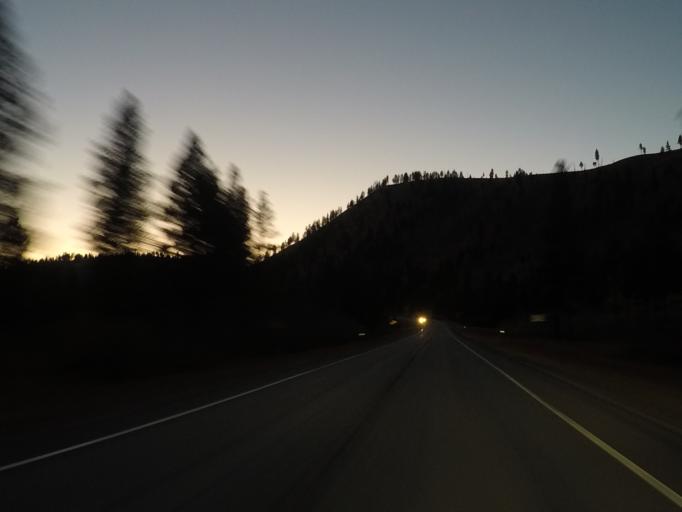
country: US
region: Montana
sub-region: Missoula County
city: Seeley Lake
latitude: 47.0241
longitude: -113.3024
